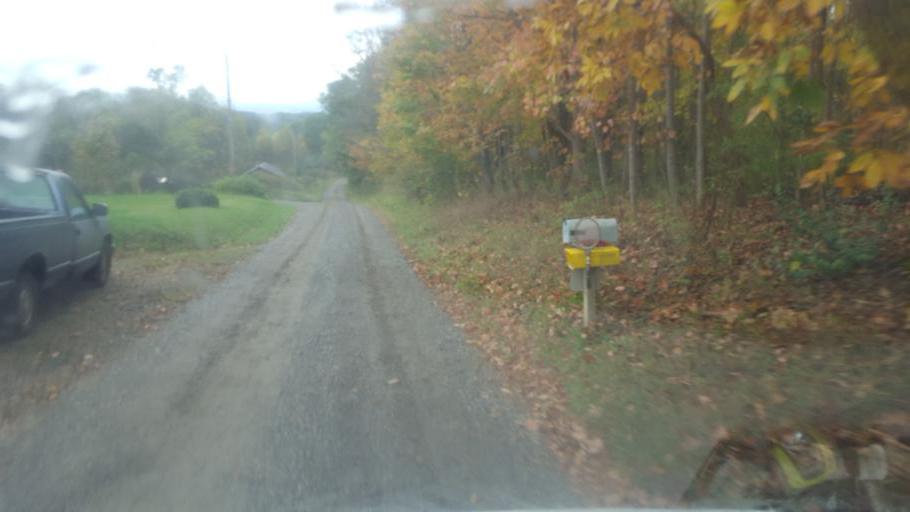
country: US
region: Ohio
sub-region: Holmes County
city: Millersburg
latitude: 40.5357
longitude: -82.0399
